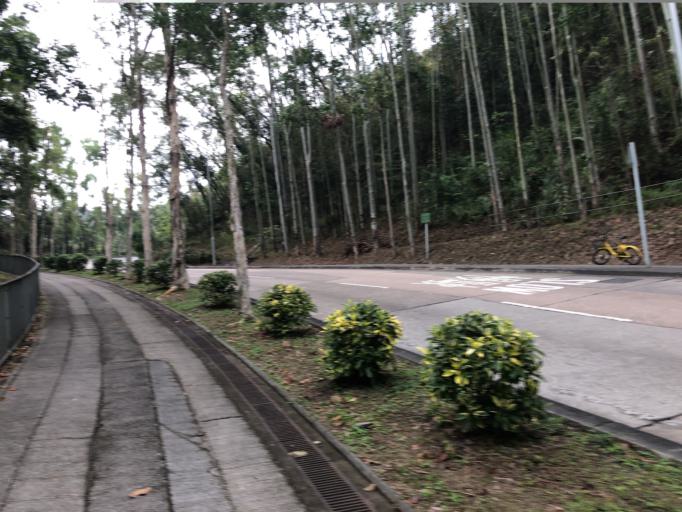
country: HK
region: Tai Po
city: Tai Po
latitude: 22.4622
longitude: 114.1922
